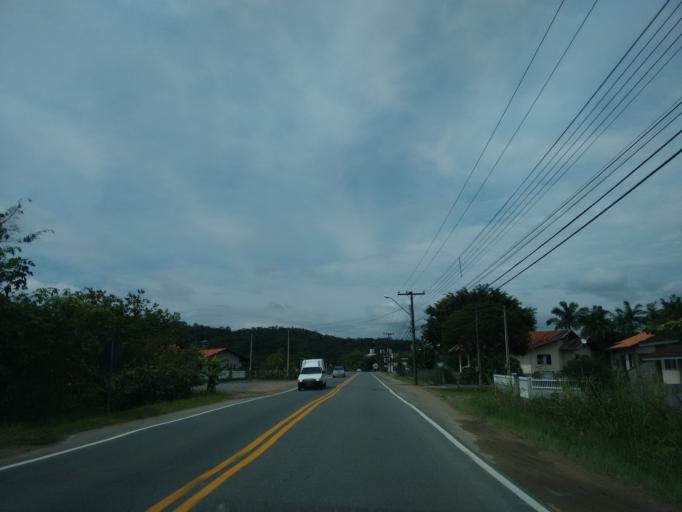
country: BR
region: Santa Catarina
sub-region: Pomerode
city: Pomerode
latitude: -26.6843
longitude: -49.1489
